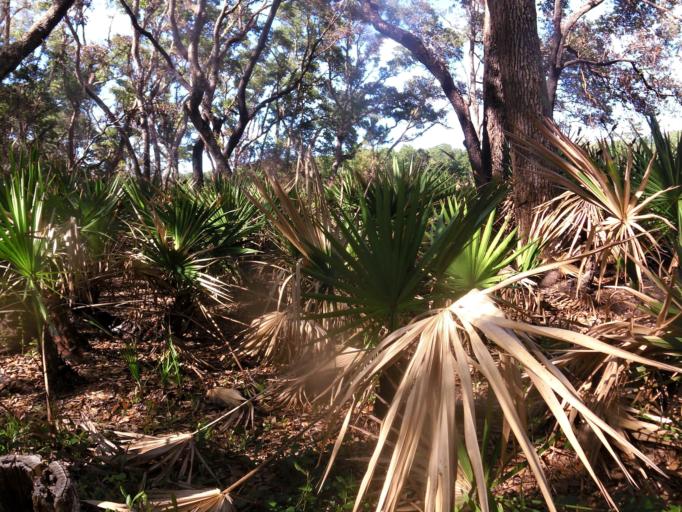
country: US
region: Florida
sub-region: Saint Johns County
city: Villano Beach
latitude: 30.0202
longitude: -81.3365
